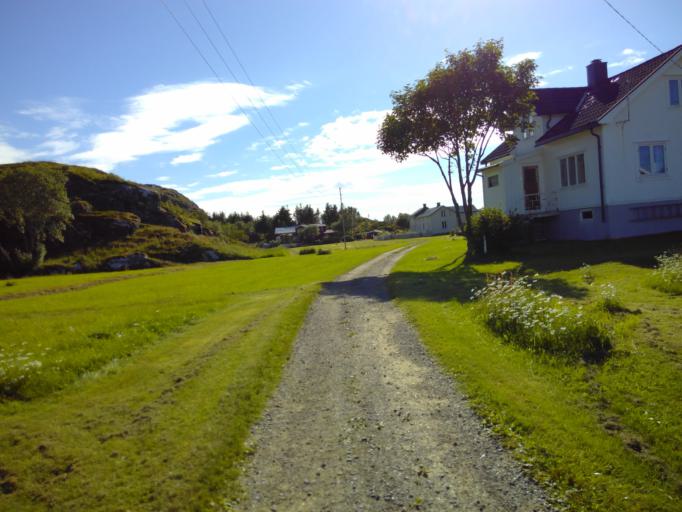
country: NO
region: Nordland
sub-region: Gildeskal
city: Inndyr
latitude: 67.2809
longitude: 13.9839
